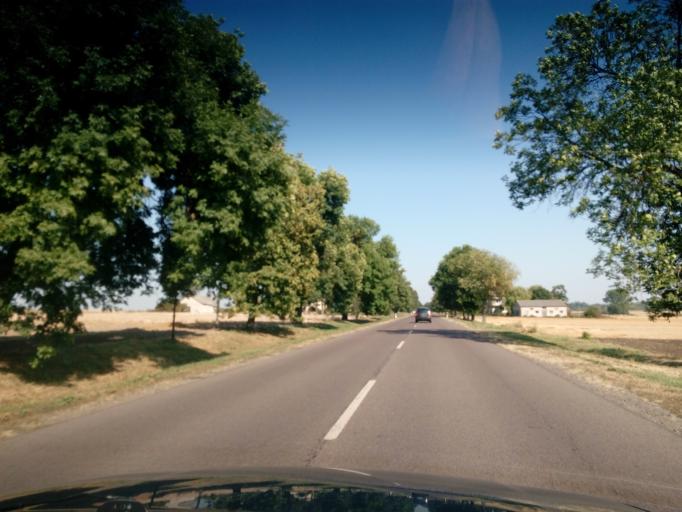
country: PL
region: Lublin Voivodeship
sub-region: Powiat hrubieszowski
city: Horodlo
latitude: 50.8492
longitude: 24.1078
